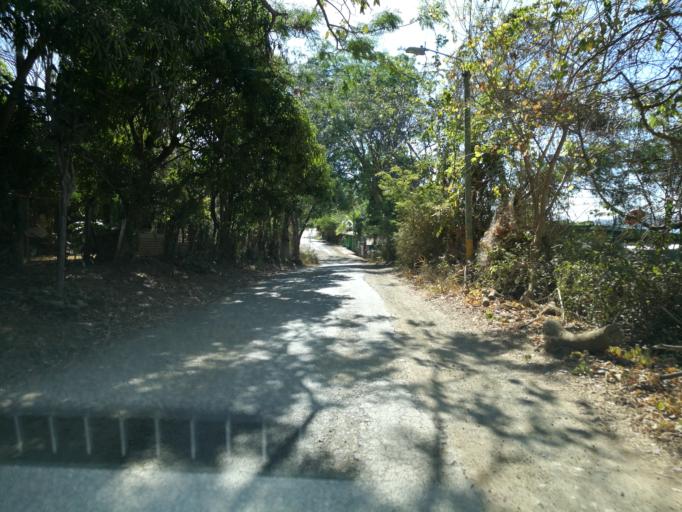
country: CR
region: Puntarenas
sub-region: Canton Central de Puntarenas
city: Puntarenas
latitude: 10.0948
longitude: -84.9788
